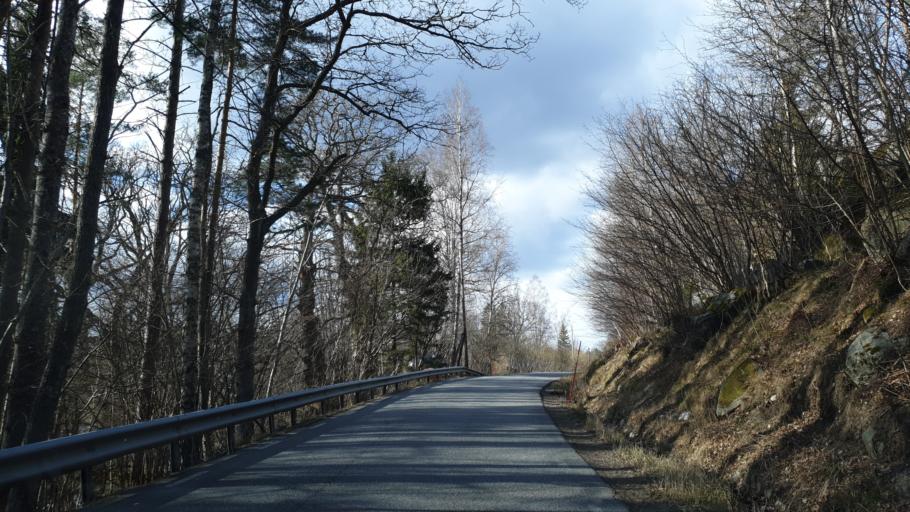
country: SE
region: Stockholm
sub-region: Tyreso Kommun
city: Brevik
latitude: 59.2437
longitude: 18.4442
